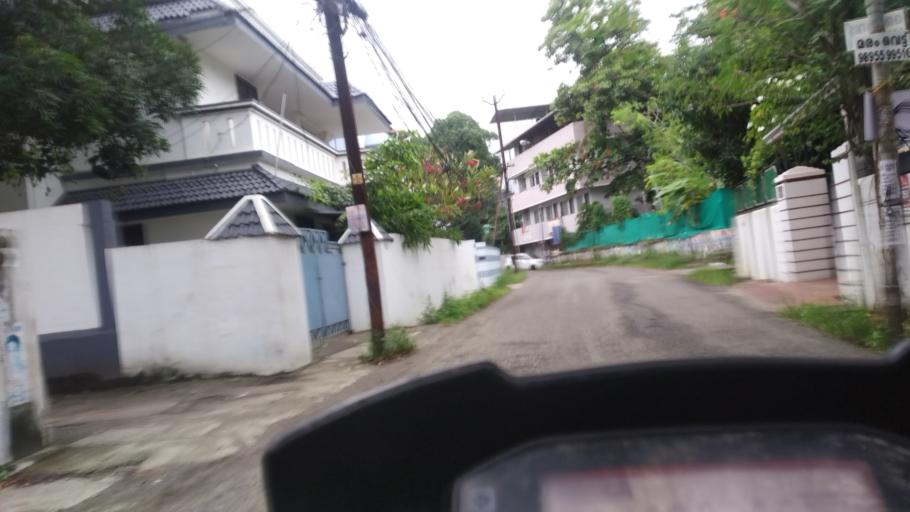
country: IN
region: Kerala
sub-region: Ernakulam
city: Cochin
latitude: 9.9859
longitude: 76.2984
